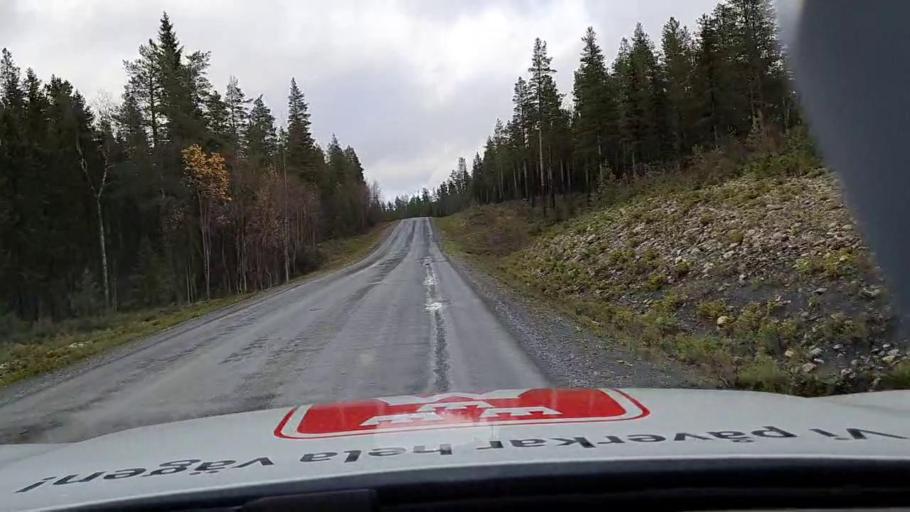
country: SE
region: Jaemtland
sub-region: Krokoms Kommun
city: Valla
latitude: 63.0737
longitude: 13.9596
